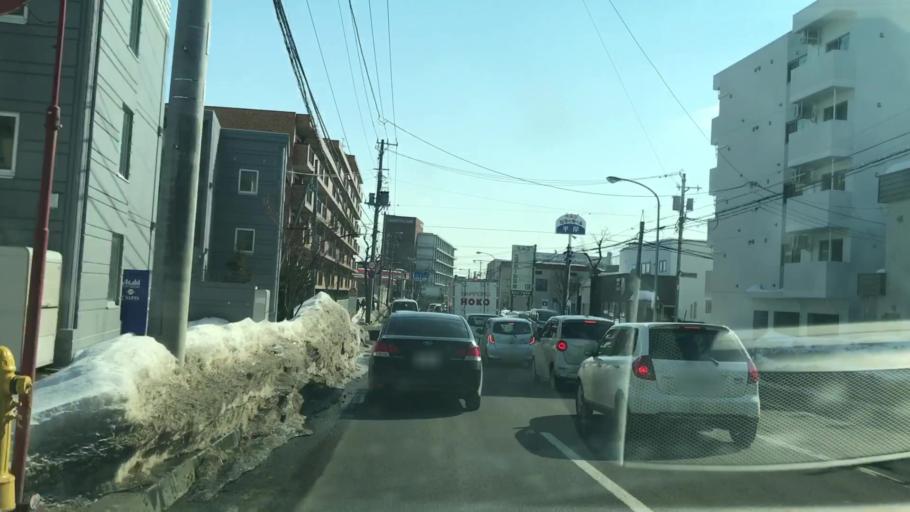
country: JP
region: Hokkaido
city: Sapporo
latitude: 43.0254
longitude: 141.3780
